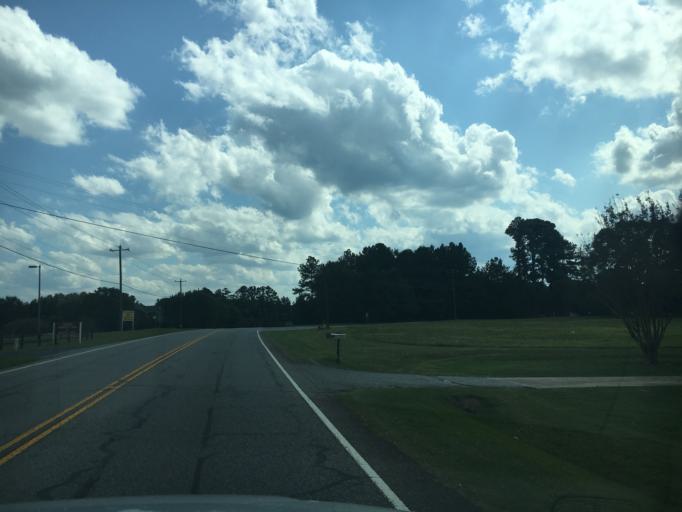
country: US
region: South Carolina
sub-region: Anderson County
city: Belton
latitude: 34.5641
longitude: -82.4896
